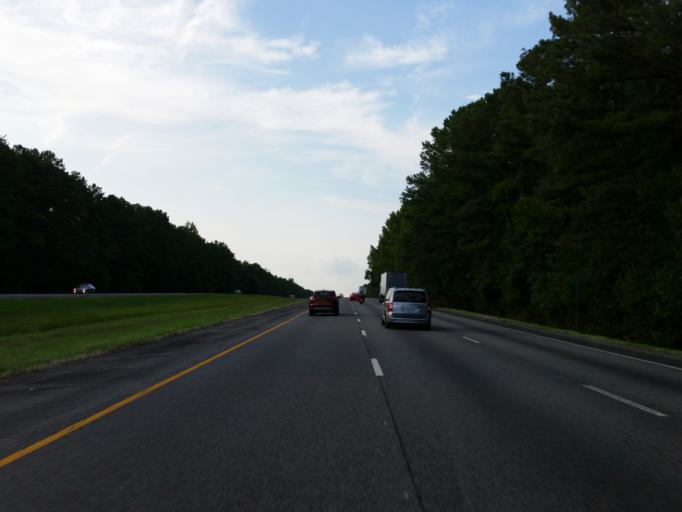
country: US
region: Georgia
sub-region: Houston County
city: Perry
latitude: 32.3669
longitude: -83.7681
